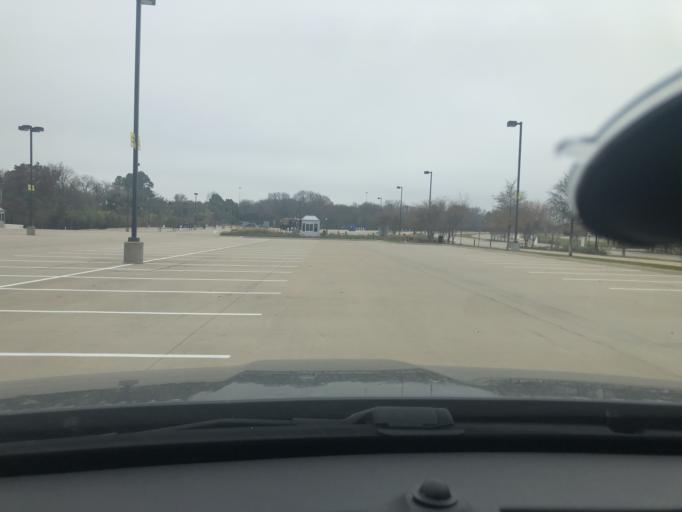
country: US
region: Texas
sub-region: Tarrant County
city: River Oaks
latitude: 32.7387
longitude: -97.3674
